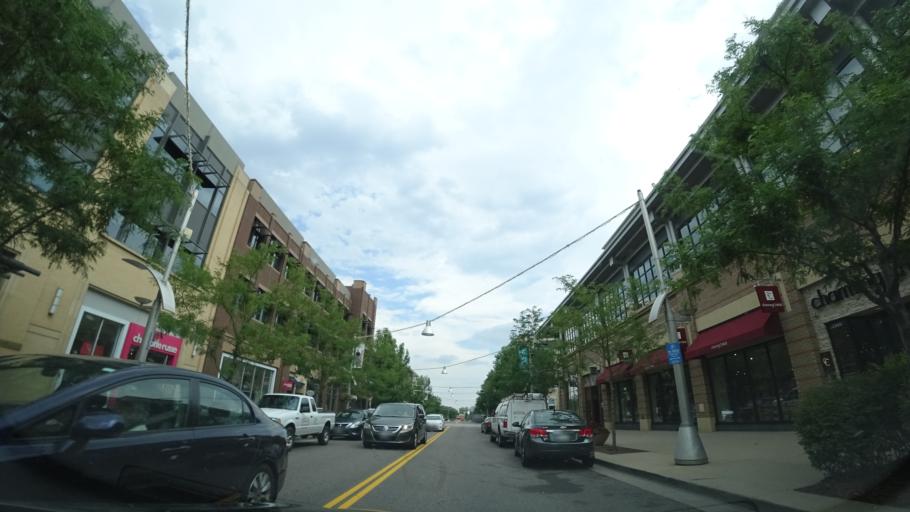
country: US
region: Colorado
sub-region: Jefferson County
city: Lakewood
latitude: 39.7093
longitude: -105.0777
